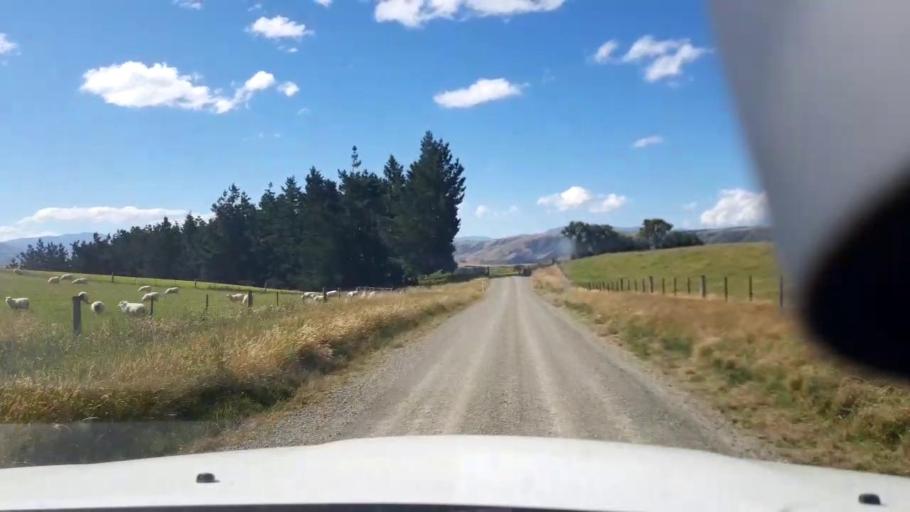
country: NZ
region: Canterbury
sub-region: Timaru District
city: Pleasant Point
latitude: -44.3158
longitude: 170.8753
